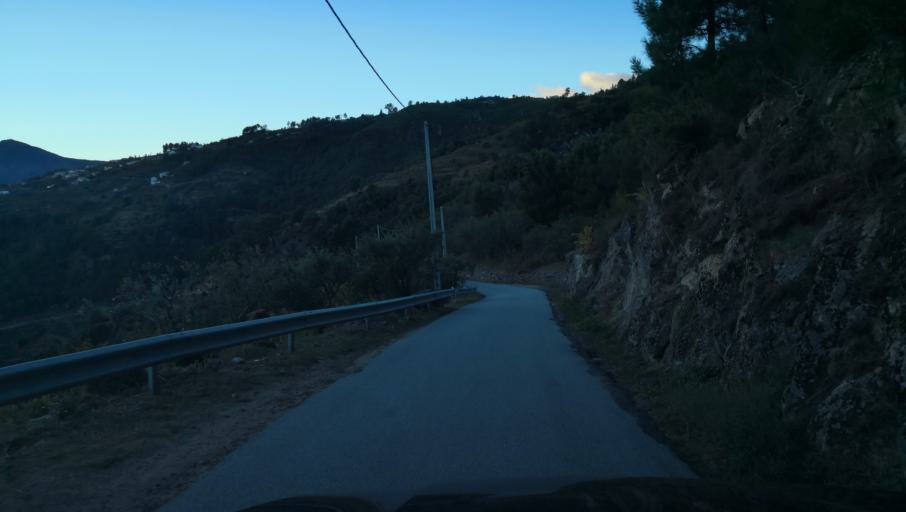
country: PT
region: Vila Real
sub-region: Santa Marta de Penaguiao
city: Santa Marta de Penaguiao
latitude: 41.2563
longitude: -7.7930
